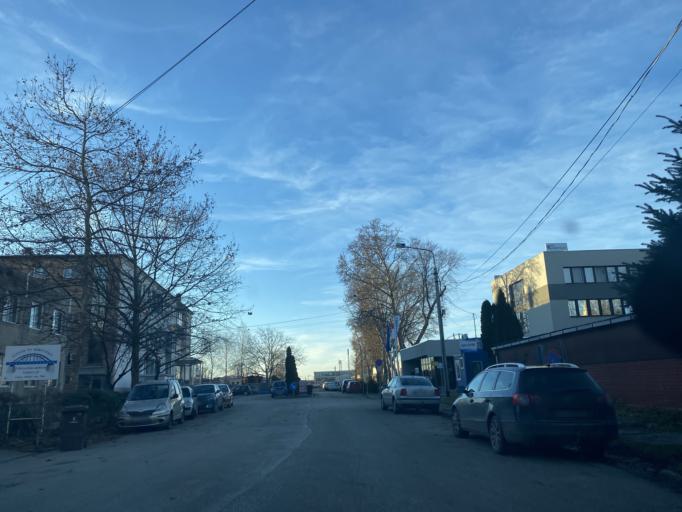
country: HU
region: Csongrad
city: Szeged
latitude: 46.2600
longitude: 20.1329
